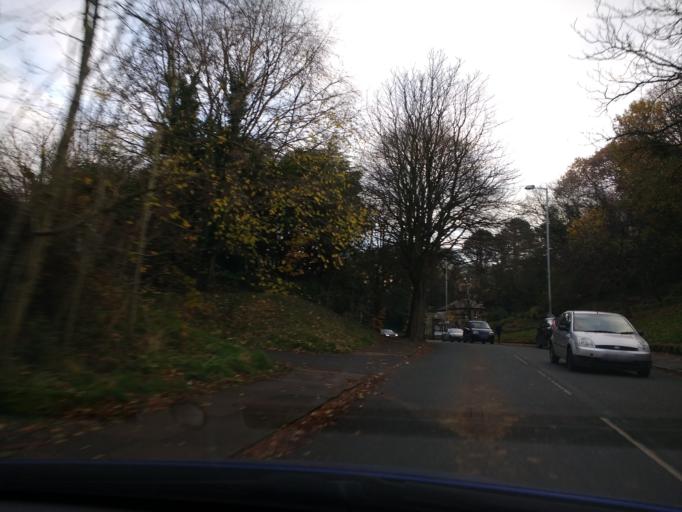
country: GB
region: England
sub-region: Lancashire
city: Lancaster
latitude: 54.0477
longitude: -2.7827
